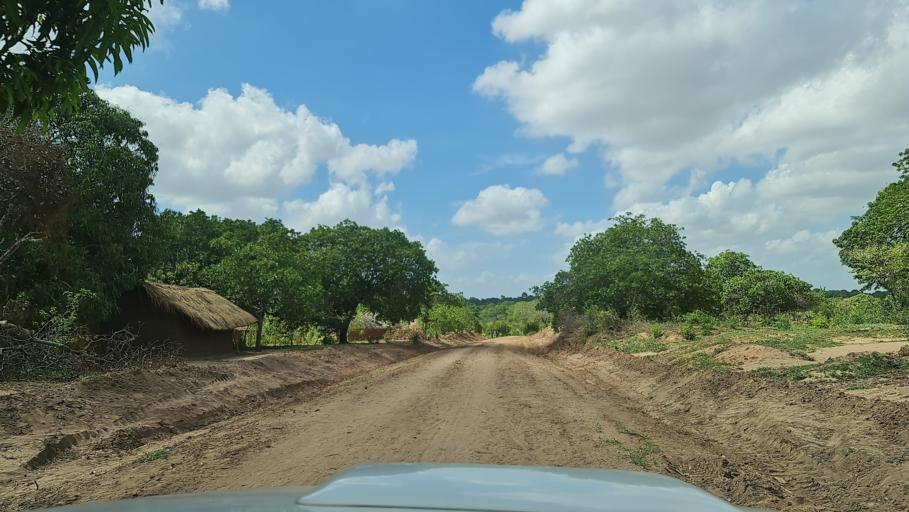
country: MZ
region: Nampula
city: Ilha de Mocambique
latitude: -15.0101
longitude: 40.5607
